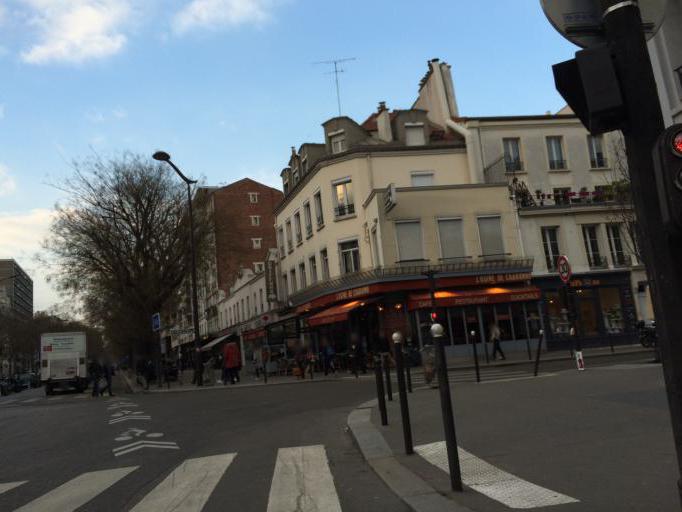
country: FR
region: Ile-de-France
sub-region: Departement du Val-de-Marne
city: Saint-Mande
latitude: 48.8512
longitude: 2.3987
